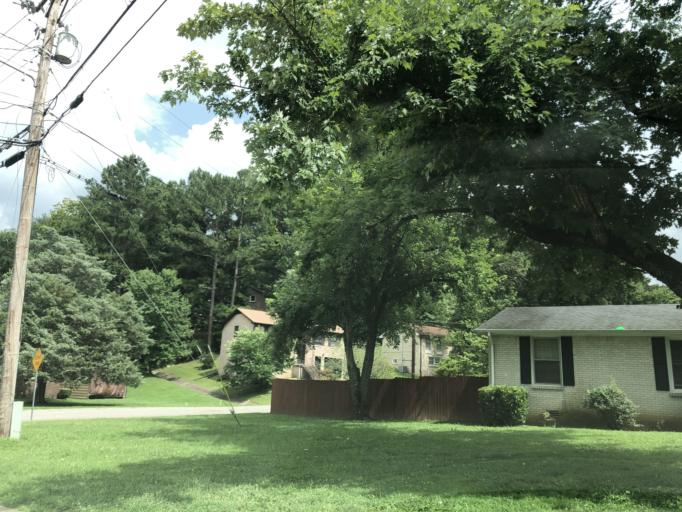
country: US
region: Tennessee
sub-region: Williamson County
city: Brentwood Estates
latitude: 36.0598
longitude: -86.6879
